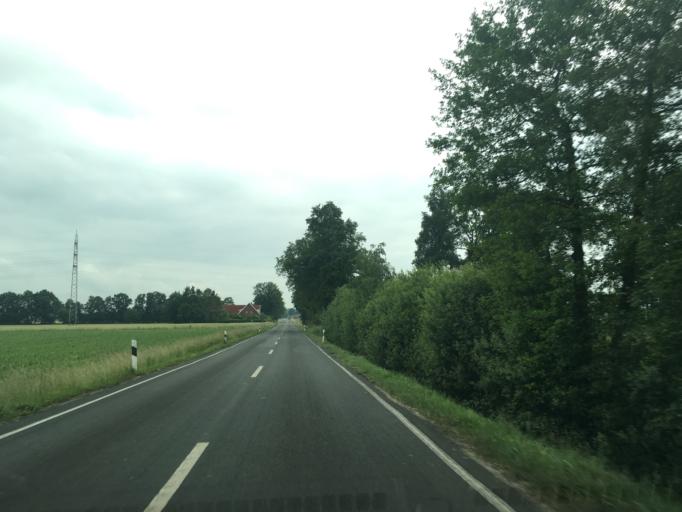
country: DE
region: North Rhine-Westphalia
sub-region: Regierungsbezirk Munster
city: Steinfurt
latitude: 52.1126
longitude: 7.3371
